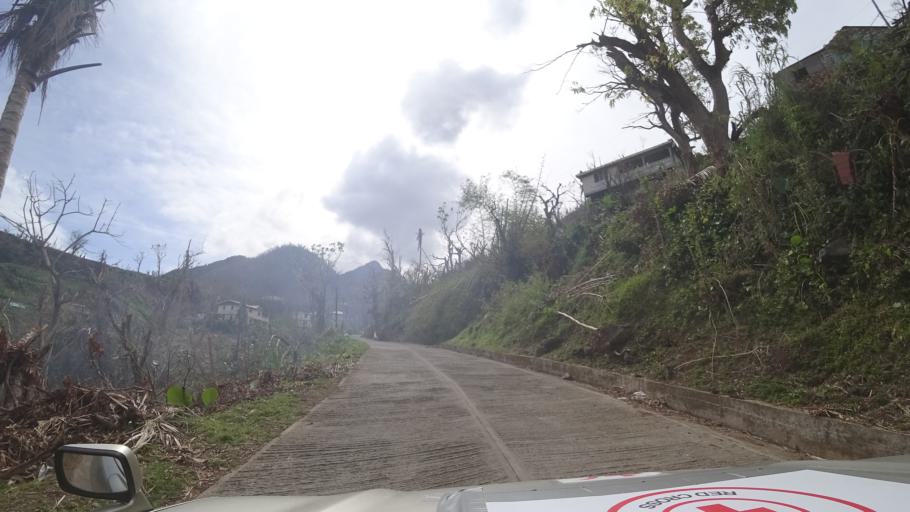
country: DM
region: Saint Patrick
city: Berekua
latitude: 15.2388
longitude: -61.3241
